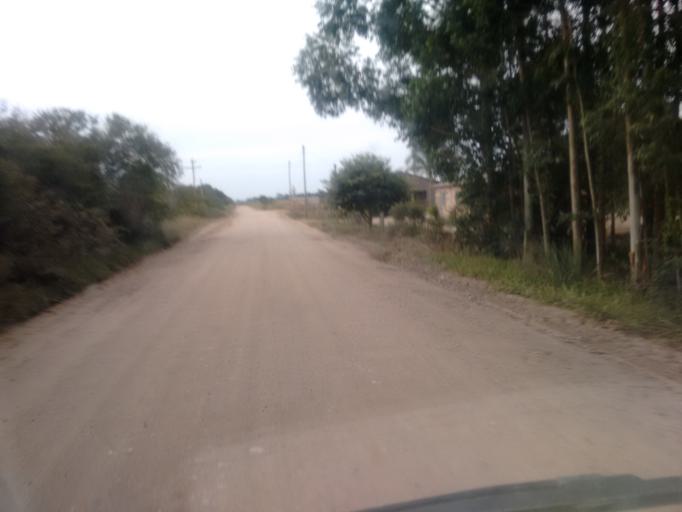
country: BR
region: Rio Grande do Sul
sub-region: Camaqua
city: Camaqua
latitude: -30.9819
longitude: -51.7958
